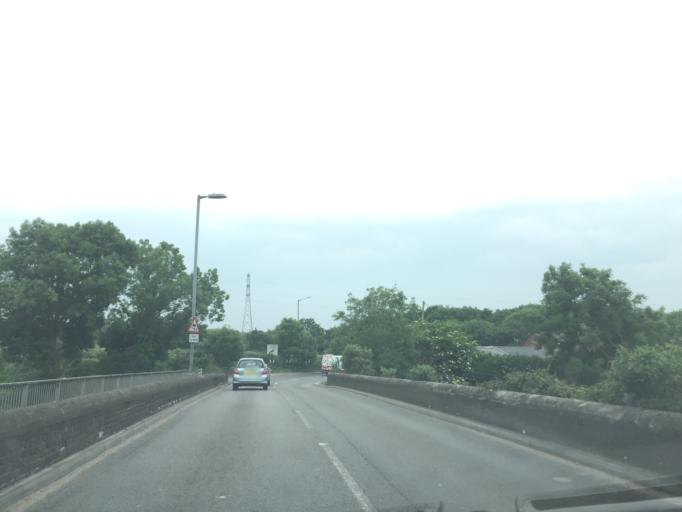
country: GB
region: England
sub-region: Dorset
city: Ferndown
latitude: 50.7753
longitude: -1.9101
